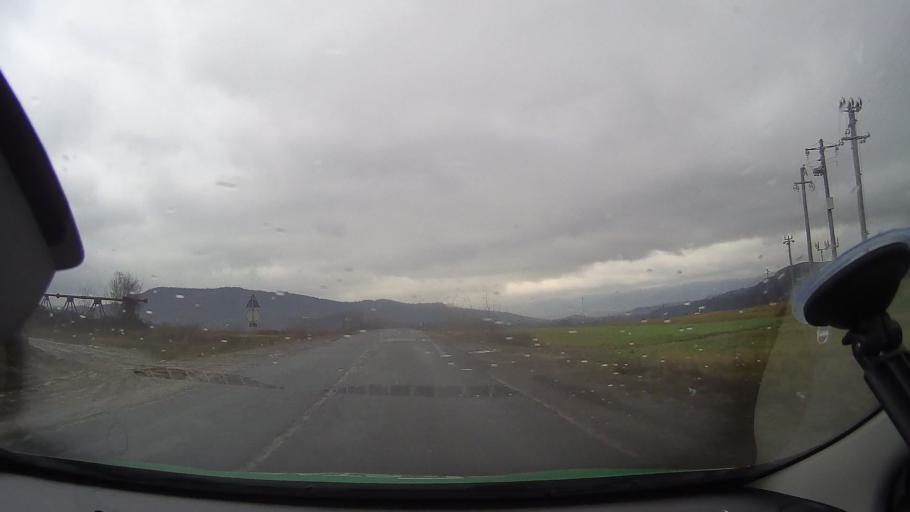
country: RO
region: Arad
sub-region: Comuna Halmagiu
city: Halmagiu
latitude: 46.2332
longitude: 22.5586
